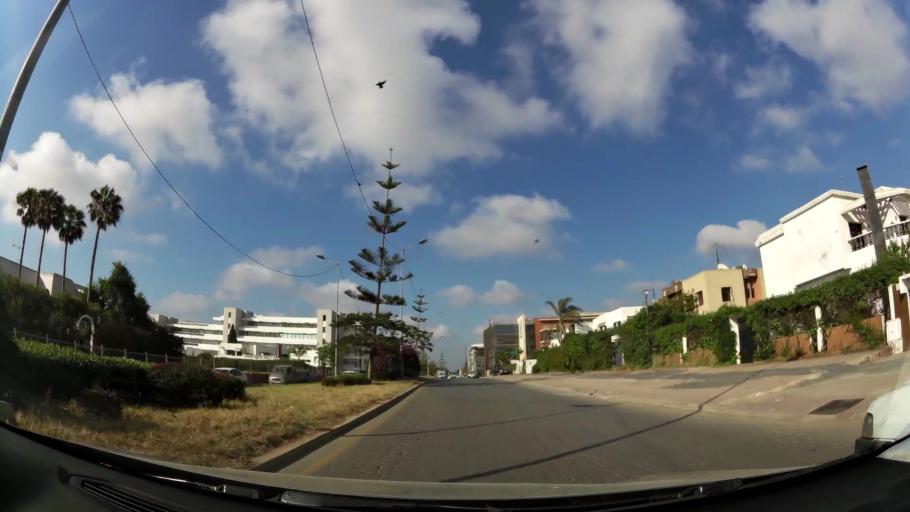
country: MA
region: Rabat-Sale-Zemmour-Zaer
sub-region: Skhirate-Temara
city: Temara
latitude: 33.9521
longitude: -6.8657
